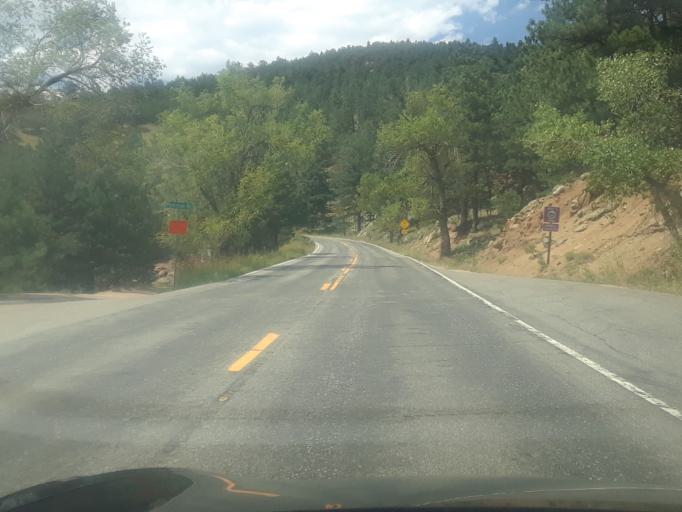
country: US
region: Colorado
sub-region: Boulder County
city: Boulder
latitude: 40.0349
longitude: -105.3245
